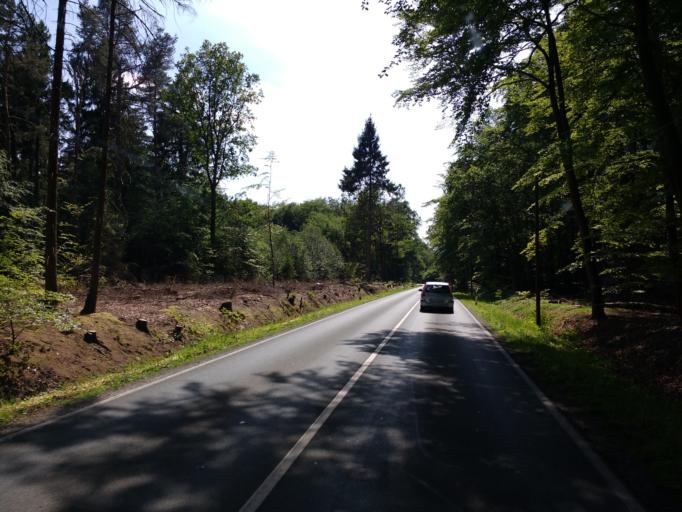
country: DE
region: Lower Saxony
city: Belm
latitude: 52.3247
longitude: 8.1143
